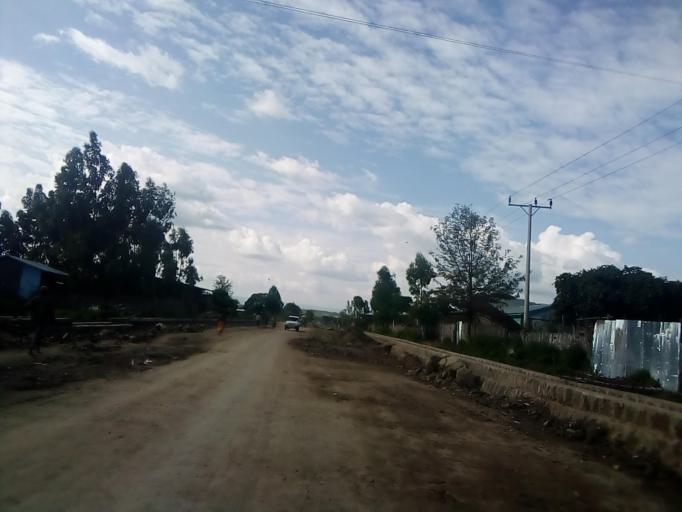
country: ET
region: Southern Nations, Nationalities, and People's Region
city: K'olito
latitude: 7.6009
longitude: 38.0670
